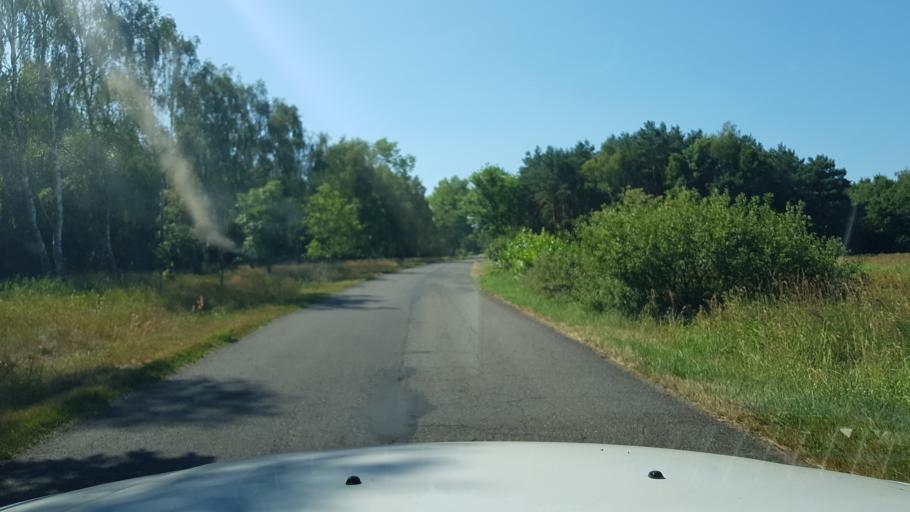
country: PL
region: West Pomeranian Voivodeship
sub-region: Powiat goleniowski
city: Goleniow
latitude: 53.4684
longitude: 14.7152
